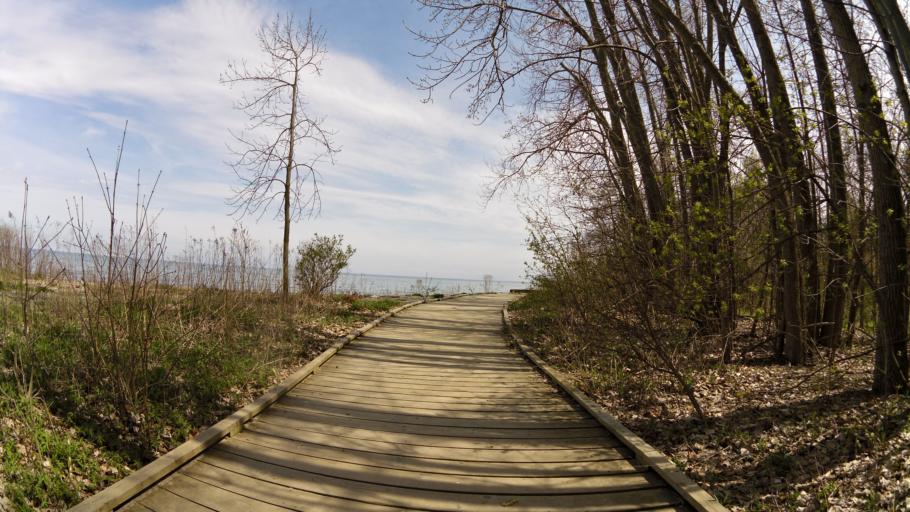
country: CA
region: Ontario
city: Mississauga
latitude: 43.5213
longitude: -79.6027
